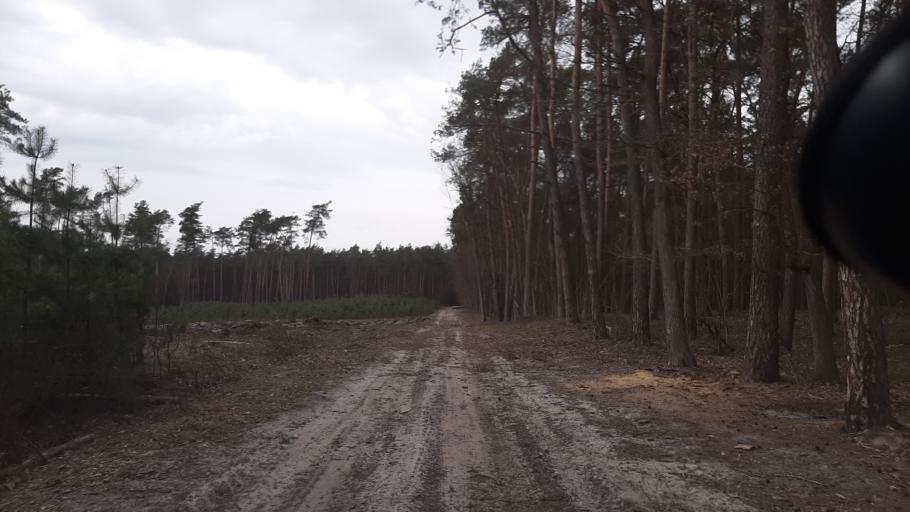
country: PL
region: Lublin Voivodeship
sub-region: Powiat lubelski
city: Garbow
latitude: 51.3971
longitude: 22.3753
